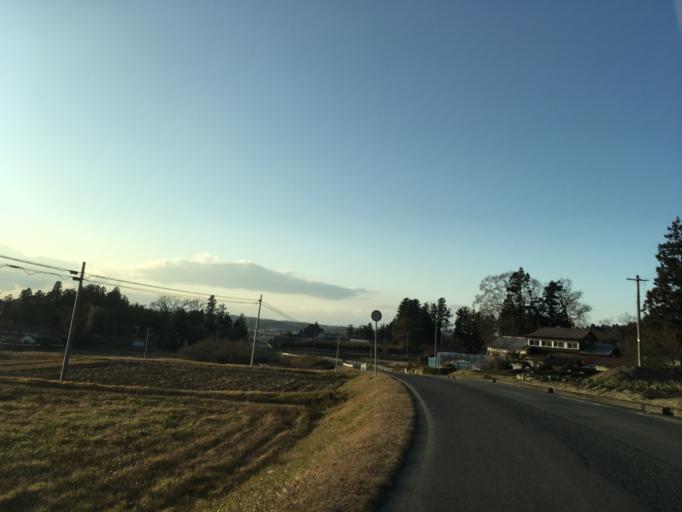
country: JP
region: Iwate
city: Ichinoseki
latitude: 38.8233
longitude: 141.2083
